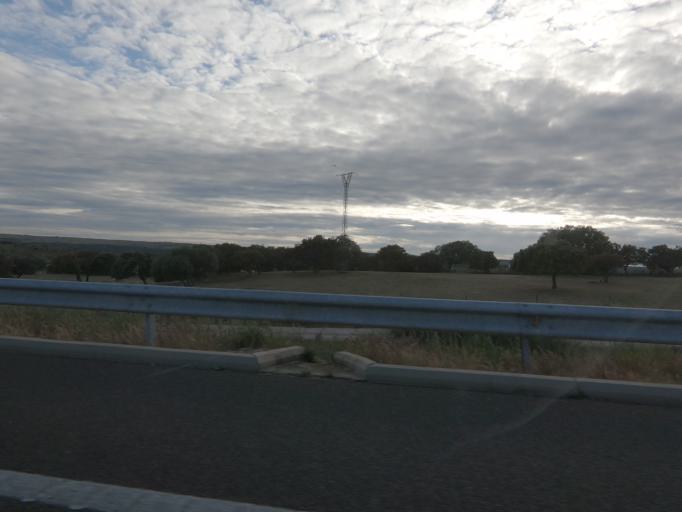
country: ES
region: Extremadura
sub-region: Provincia de Caceres
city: Santiago del Campo
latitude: 39.6402
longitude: -6.3941
